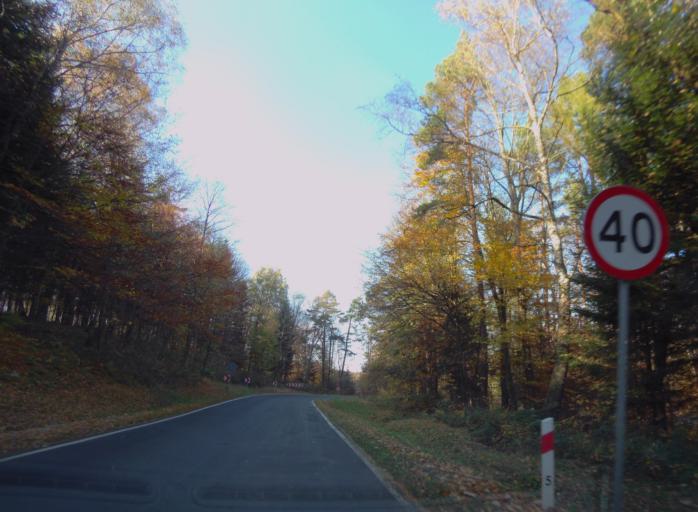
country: PL
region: Subcarpathian Voivodeship
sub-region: Powiat leski
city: Polanczyk
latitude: 49.3951
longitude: 22.4347
